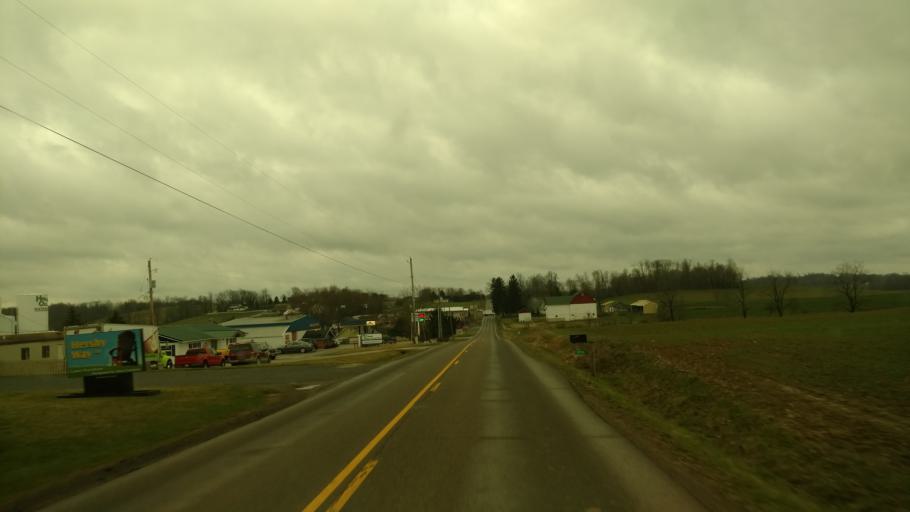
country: US
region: Ohio
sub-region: Holmes County
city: Millersburg
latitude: 40.5721
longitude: -81.8207
